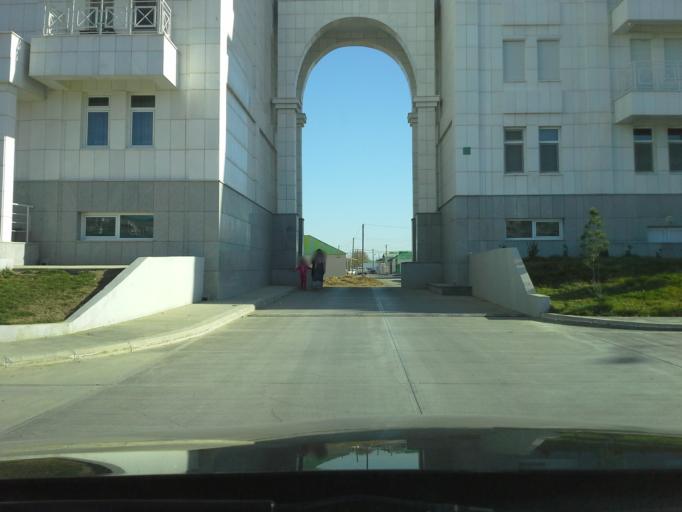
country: TM
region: Ahal
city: Ashgabat
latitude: 37.9747
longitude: 58.3425
